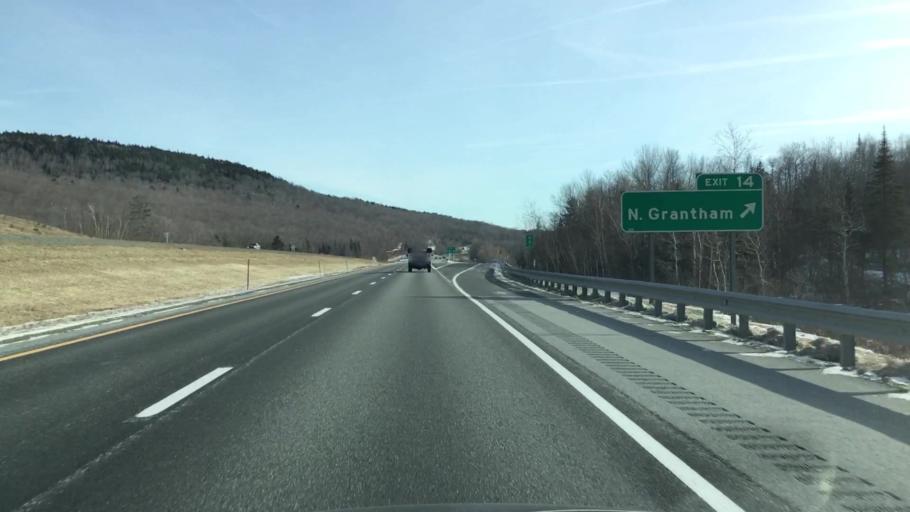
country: US
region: New Hampshire
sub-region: Grafton County
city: Enfield
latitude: 43.5694
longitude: -72.1534
